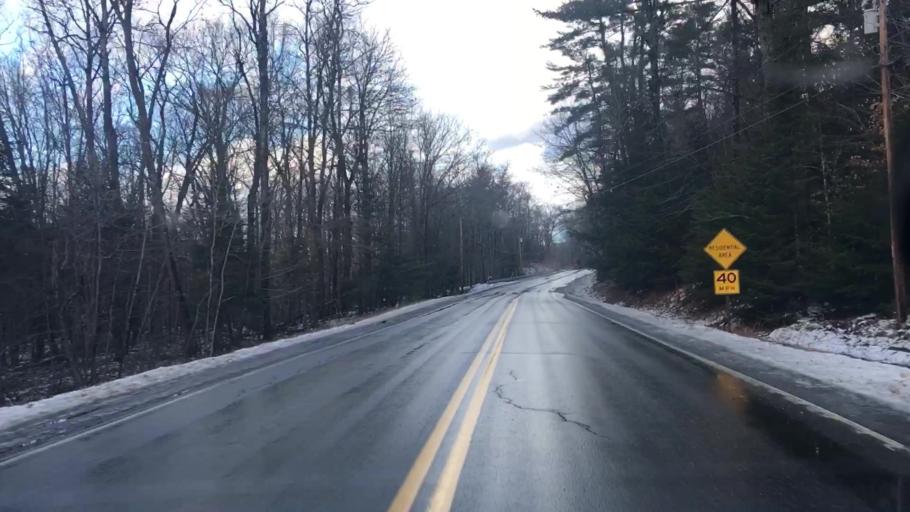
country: US
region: Maine
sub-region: Hancock County
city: Dedham
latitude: 44.6511
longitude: -68.6852
